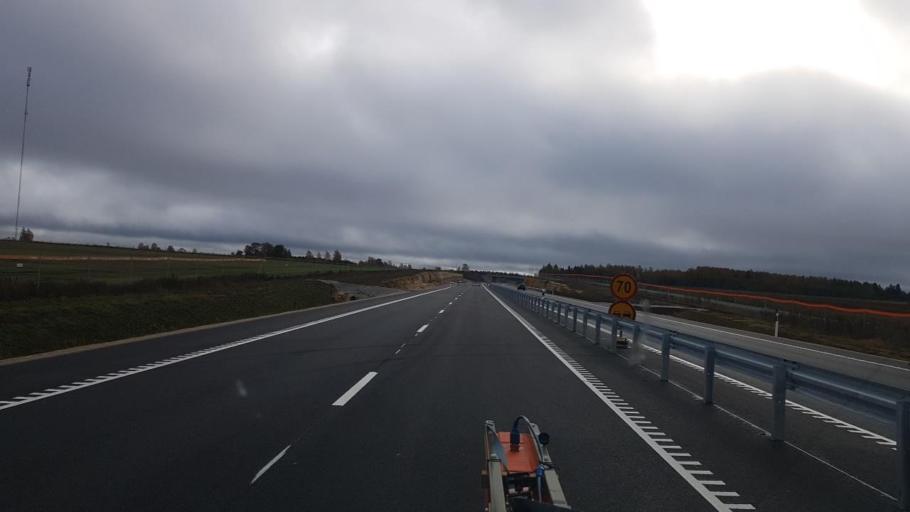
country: EE
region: Jaervamaa
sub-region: Paide linn
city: Paide
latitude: 58.9980
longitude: 25.5809
